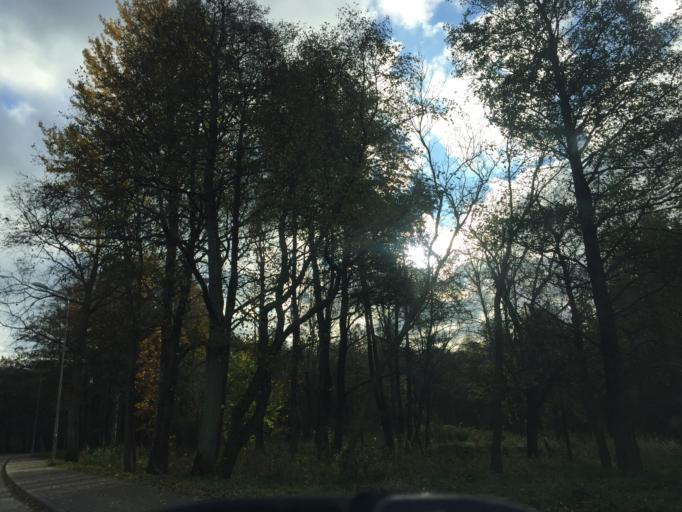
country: LV
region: Liepaja
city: Vec-Liepaja
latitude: 56.5470
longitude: 21.0787
